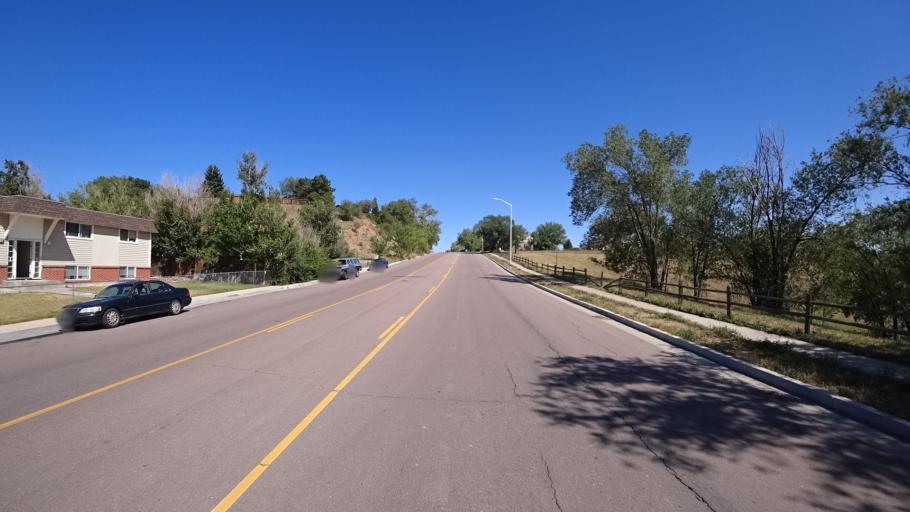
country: US
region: Colorado
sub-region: El Paso County
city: Colorado Springs
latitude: 38.8557
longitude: -104.8560
